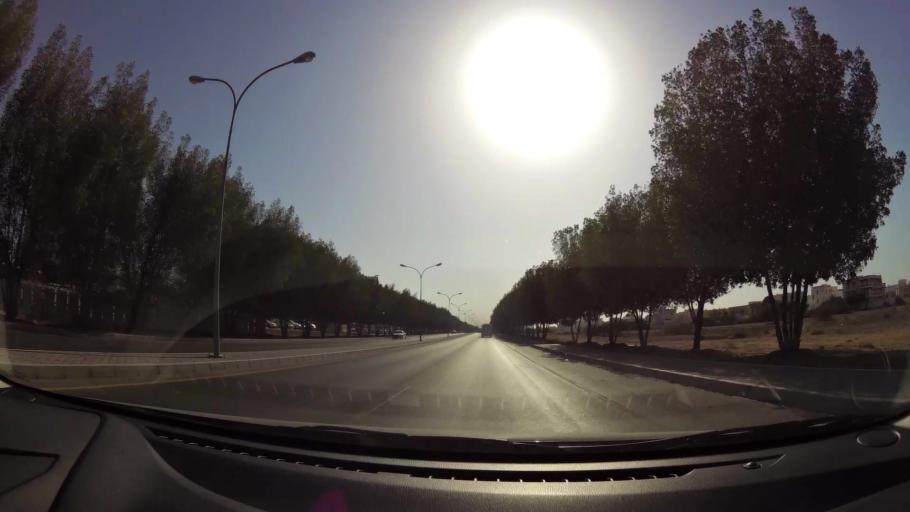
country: OM
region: Muhafazat Masqat
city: As Sib al Jadidah
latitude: 23.6155
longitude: 58.2065
